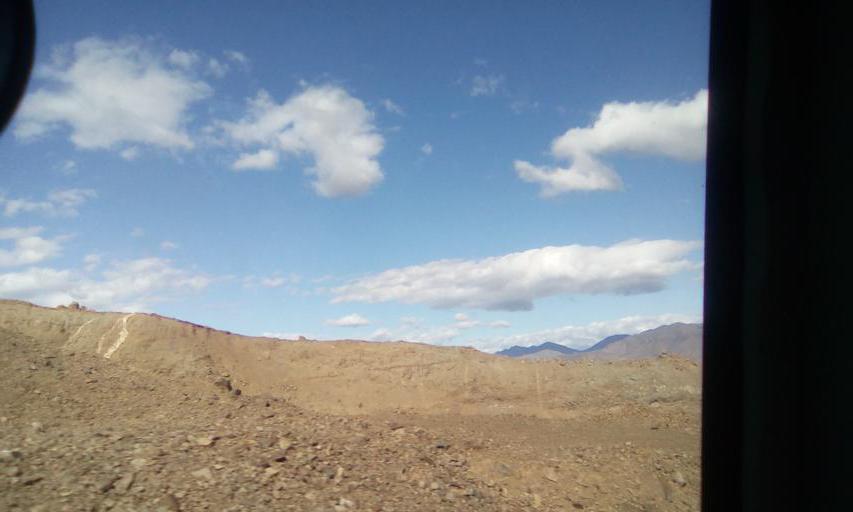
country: LS
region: Qacha's Nek
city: Qacha's Nek
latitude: -30.0428
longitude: 28.2745
